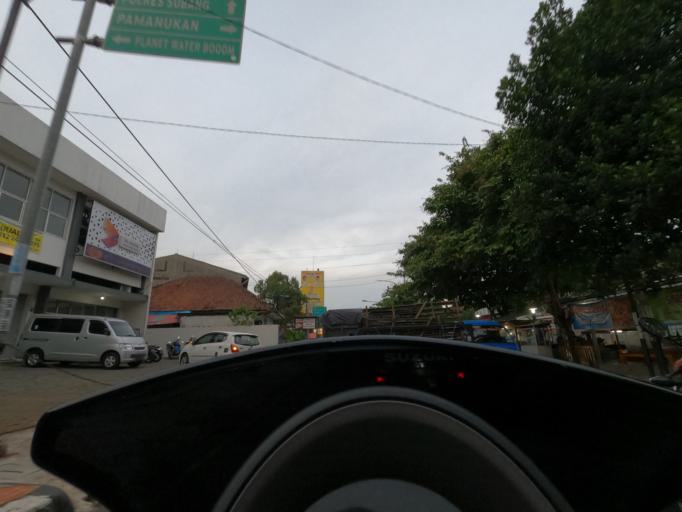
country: ID
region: West Java
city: Lembang
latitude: -6.5732
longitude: 107.7579
